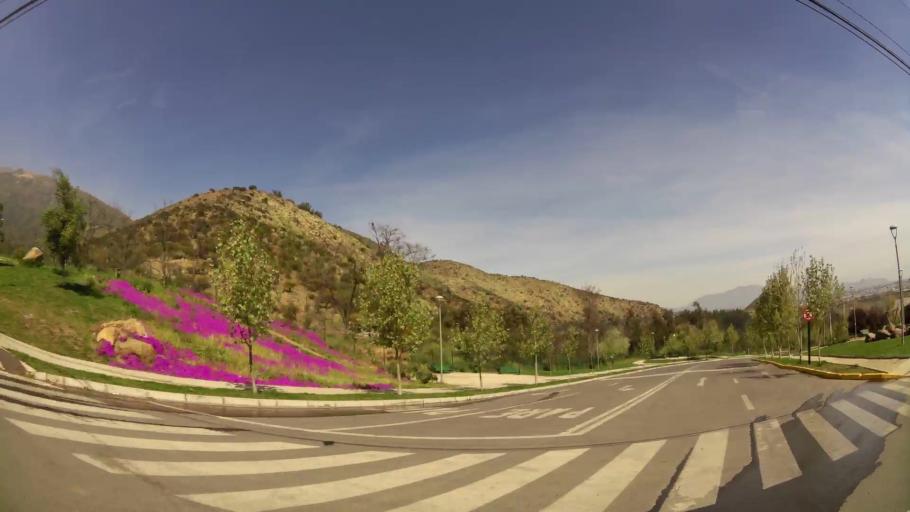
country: CL
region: Santiago Metropolitan
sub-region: Provincia de Cordillera
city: Puente Alto
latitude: -33.5367
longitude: -70.5399
